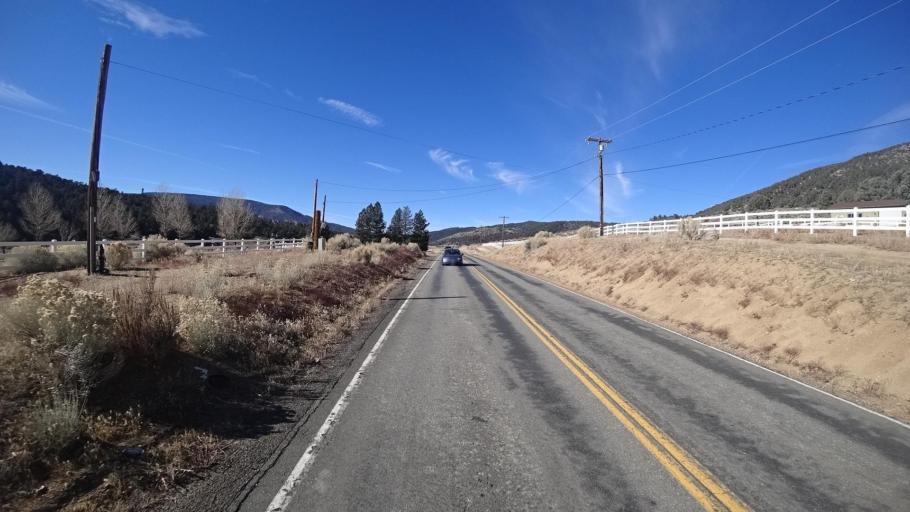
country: US
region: California
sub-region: Kern County
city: Frazier Park
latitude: 34.8299
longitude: -119.0261
